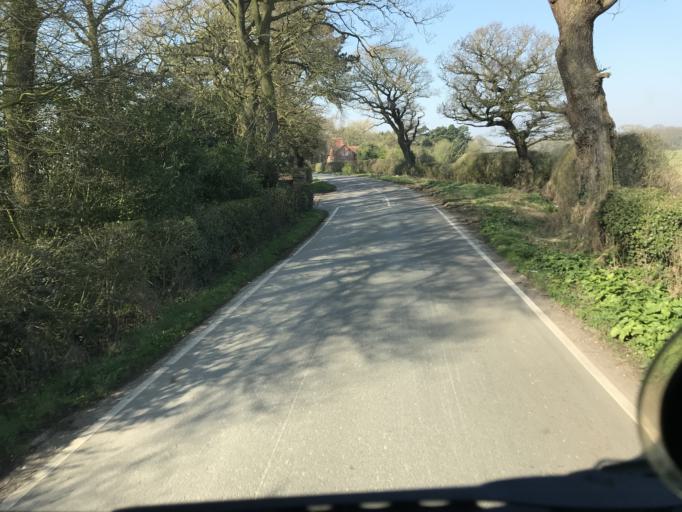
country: GB
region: England
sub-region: Cheshire West and Chester
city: Aldford
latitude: 53.1383
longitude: -2.8336
